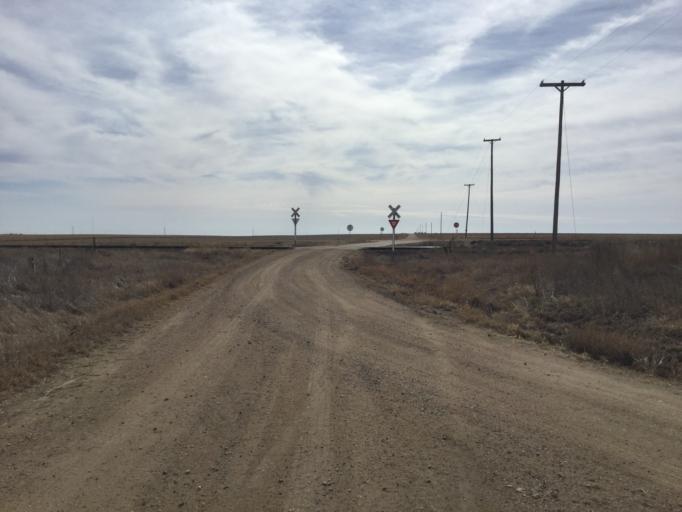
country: US
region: Kansas
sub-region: Ellis County
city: Victoria
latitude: 38.8428
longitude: -99.1700
